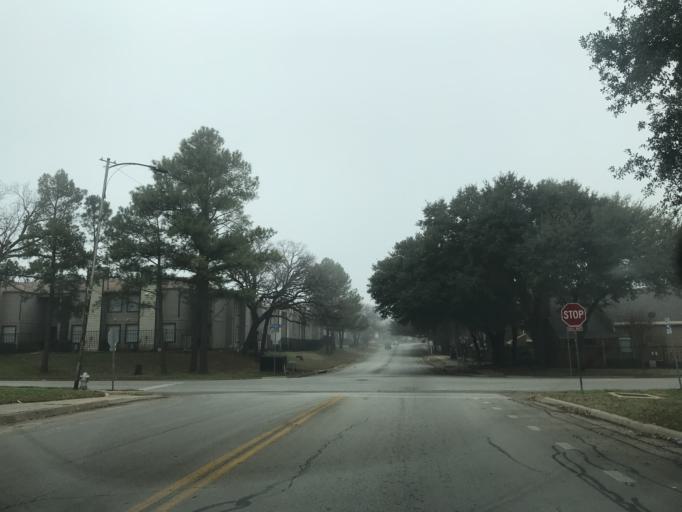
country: US
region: Texas
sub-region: Tarrant County
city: Arlington
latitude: 32.7700
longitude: -97.1052
